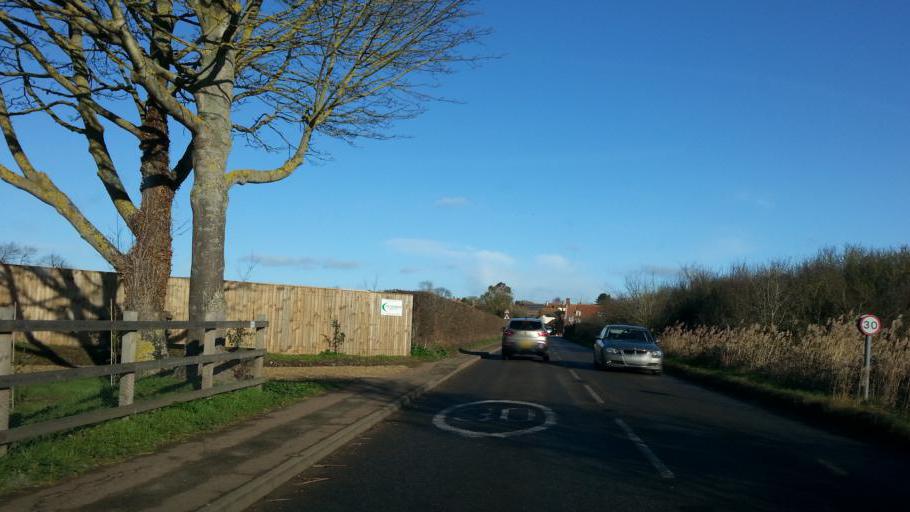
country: GB
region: England
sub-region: Suffolk
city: Saxmundham
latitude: 52.1674
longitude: 1.4979
